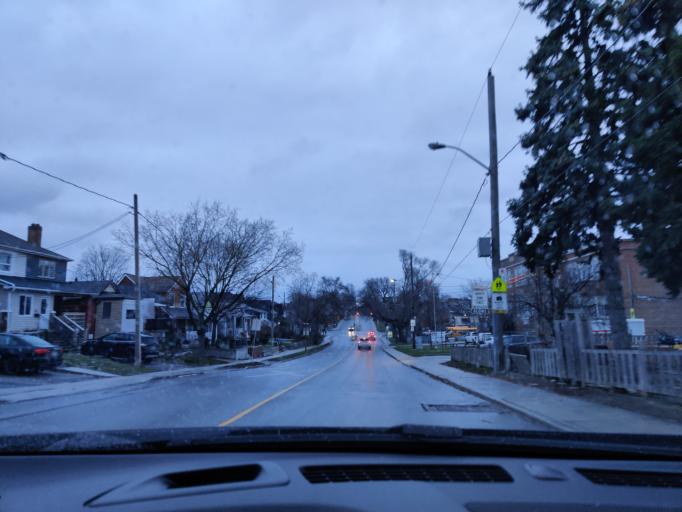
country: CA
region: Ontario
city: Toronto
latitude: 43.6846
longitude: -79.4587
